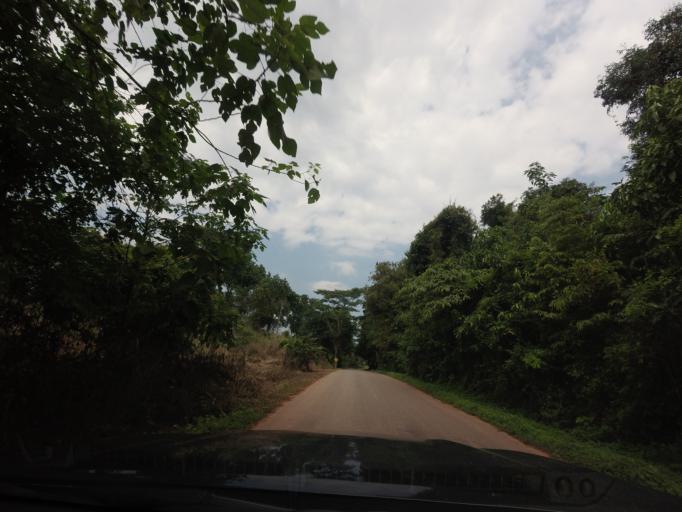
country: TH
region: Uttaradit
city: Fak Tha
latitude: 17.7886
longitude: 100.9267
